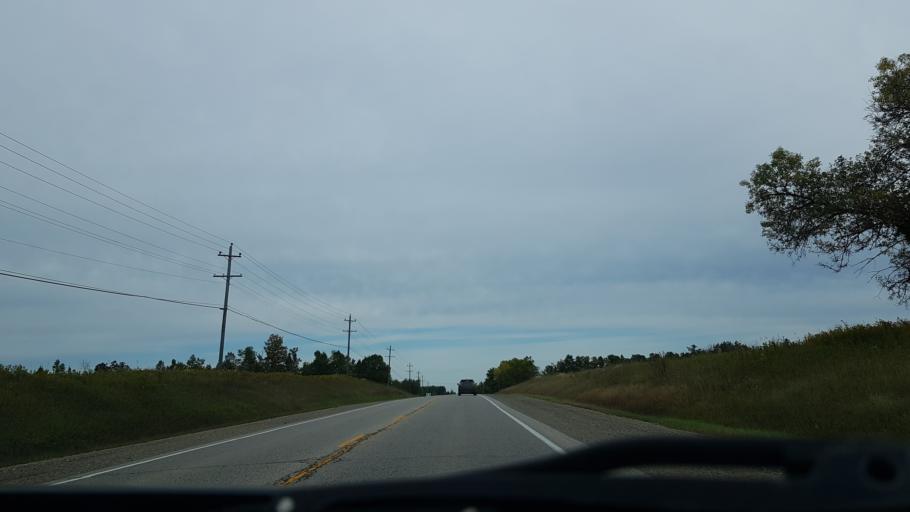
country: CA
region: Ontario
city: Orangeville
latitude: 43.7971
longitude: -80.0654
